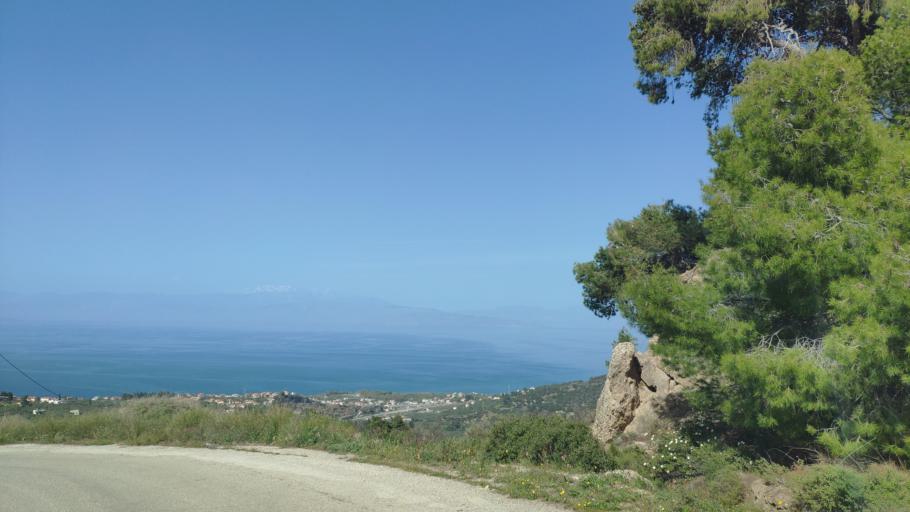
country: GR
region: West Greece
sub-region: Nomos Achaias
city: Aiyira
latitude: 38.1284
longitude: 22.3452
